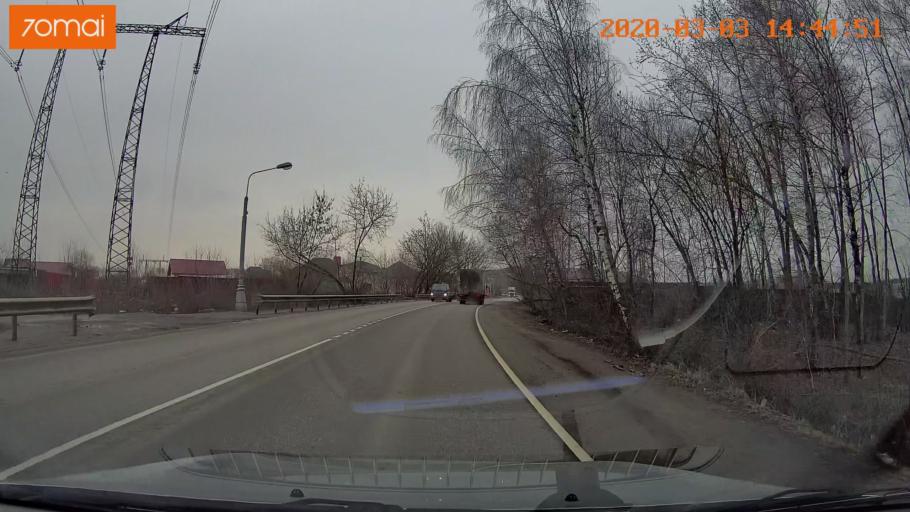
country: RU
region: Moskovskaya
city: Korenevo
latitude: 55.7016
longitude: 38.0374
